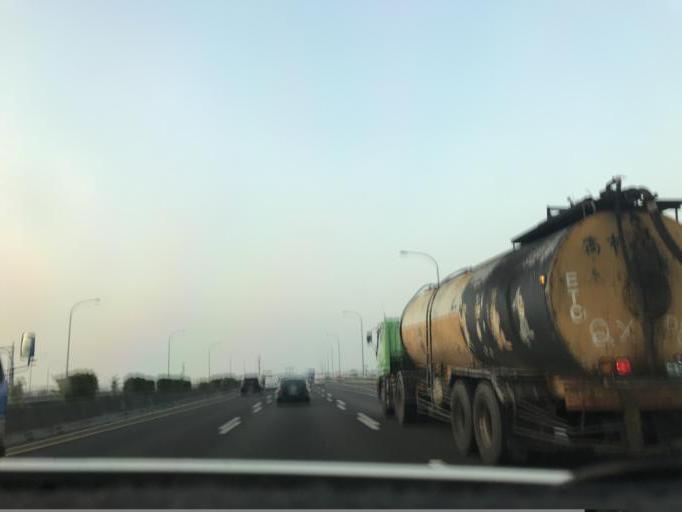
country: TW
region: Taiwan
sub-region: Yunlin
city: Douliu
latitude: 23.7323
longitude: 120.4718
